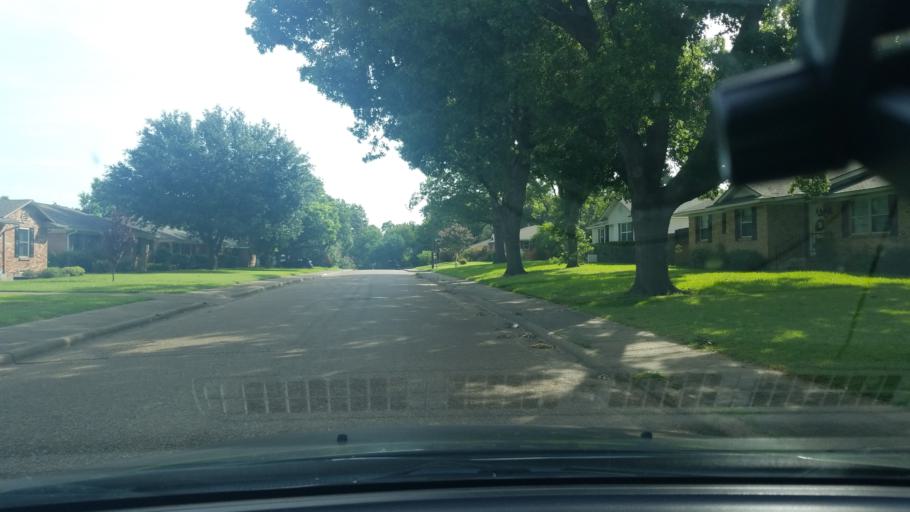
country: US
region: Texas
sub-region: Dallas County
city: Highland Park
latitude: 32.7979
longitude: -96.7052
